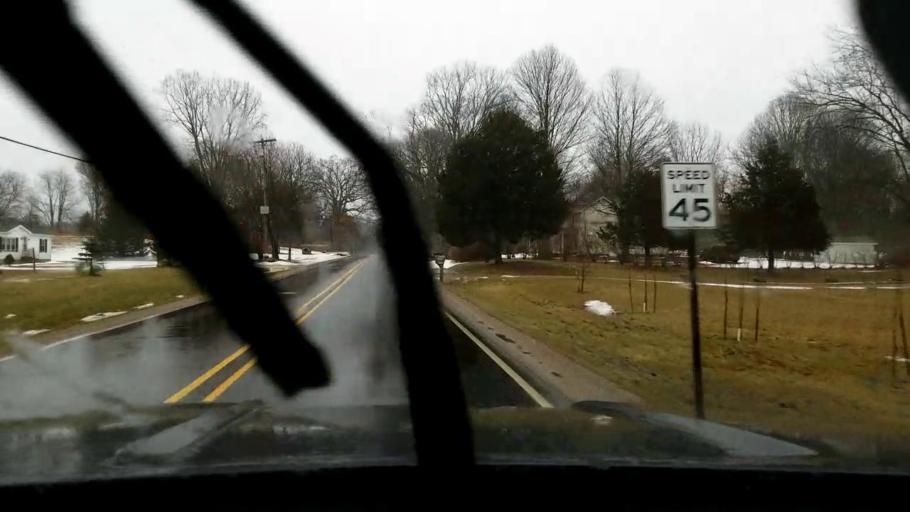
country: US
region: Michigan
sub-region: Jackson County
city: Michigan Center
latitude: 42.2843
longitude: -84.3383
